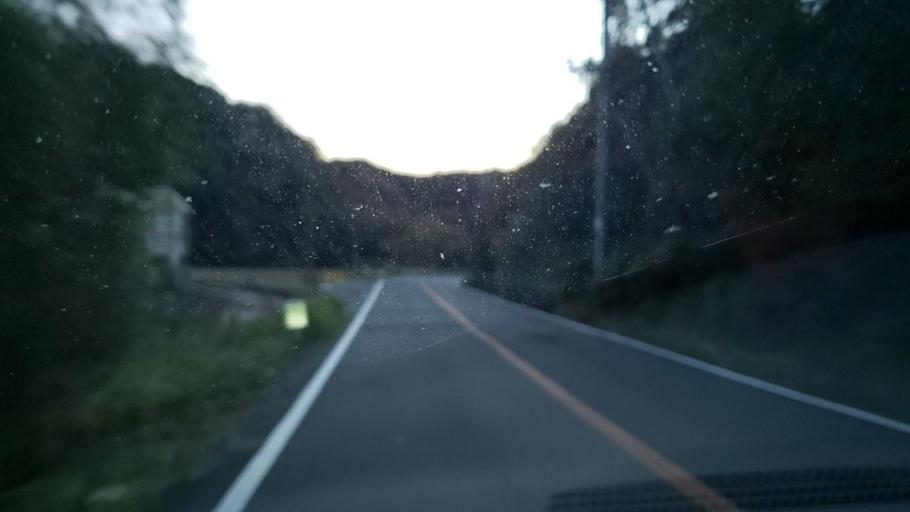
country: JP
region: Hyogo
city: Fukura
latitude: 34.2799
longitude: 134.7036
